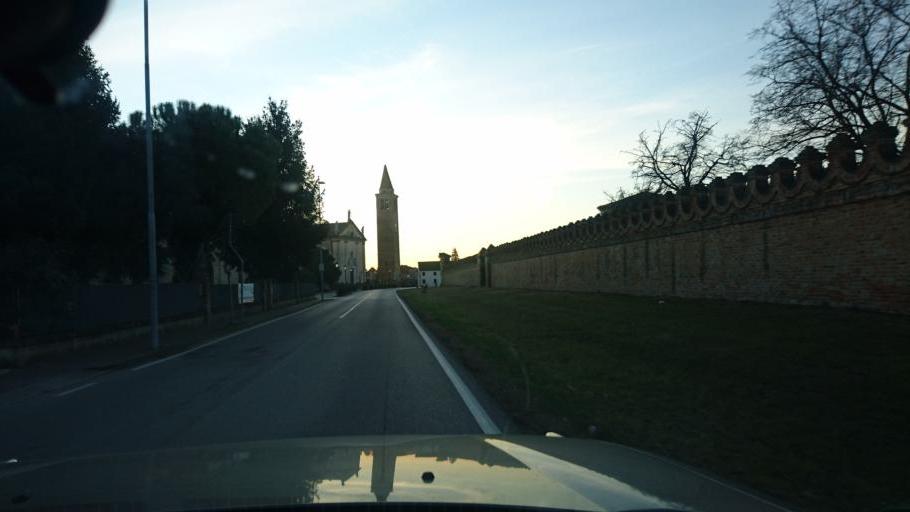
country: IT
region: Veneto
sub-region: Provincia di Padova
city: Candiana
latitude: 45.2169
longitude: 11.9627
